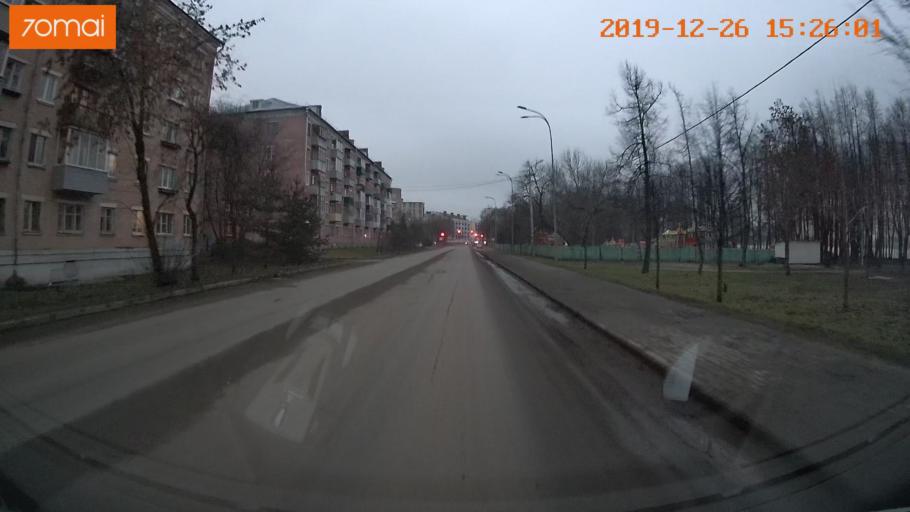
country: RU
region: Jaroslavl
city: Rybinsk
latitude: 58.0556
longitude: 38.8323
